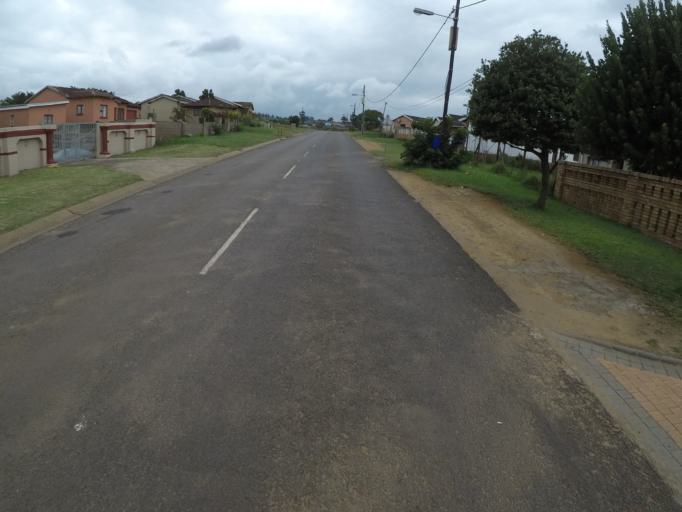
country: ZA
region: KwaZulu-Natal
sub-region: uThungulu District Municipality
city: Empangeni
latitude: -28.7812
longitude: 31.8500
